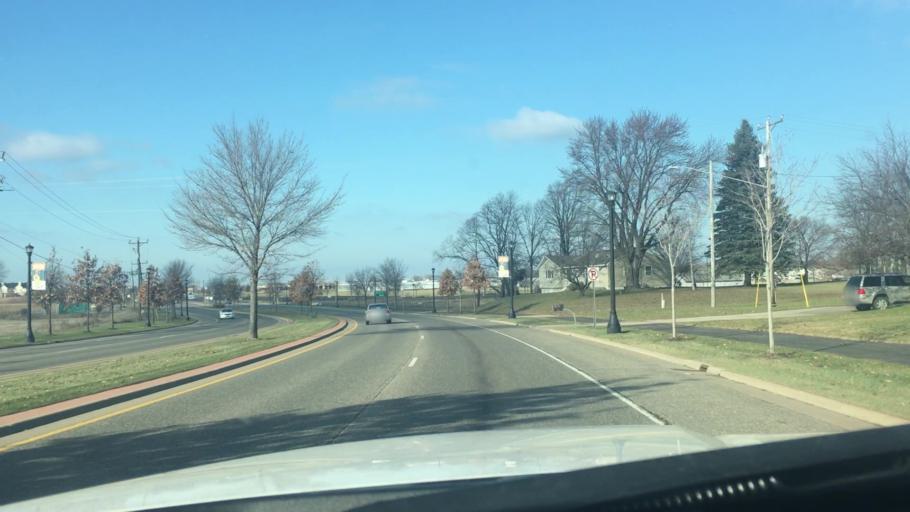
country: US
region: Minnesota
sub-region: Washington County
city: Hugo
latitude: 45.1605
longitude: -93.0004
